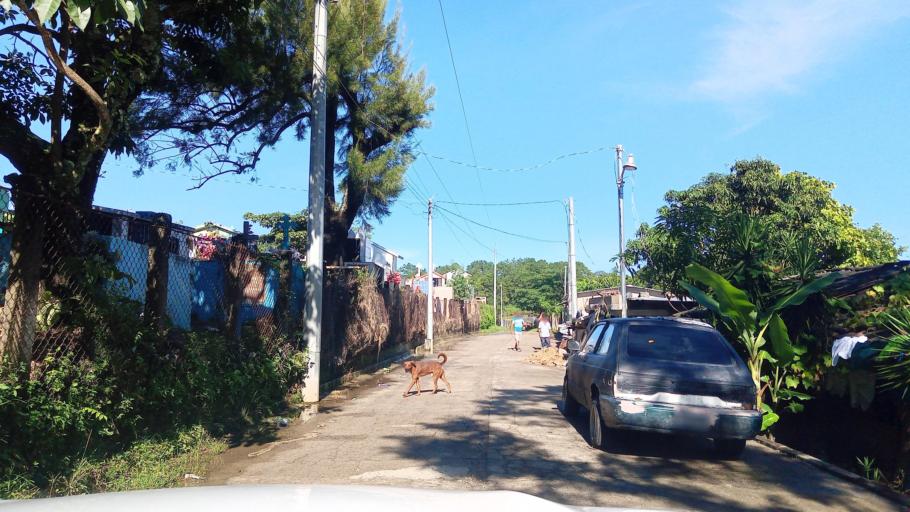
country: HN
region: Ocotepeque
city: Antigua Ocotepeque
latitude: 14.3173
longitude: -89.1768
